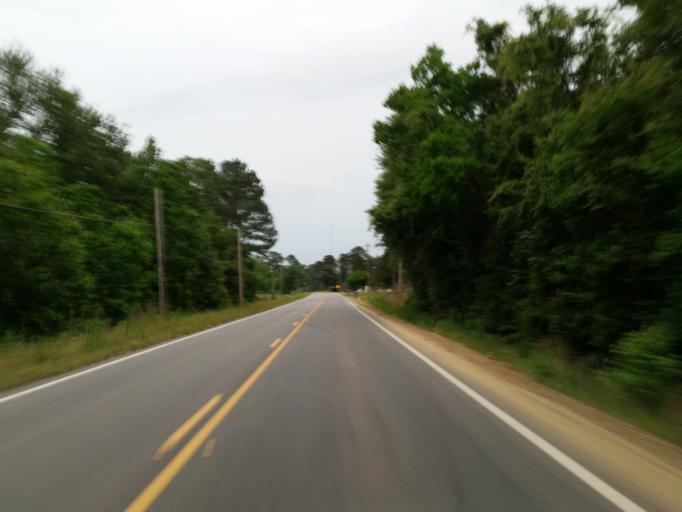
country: US
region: Georgia
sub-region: Crisp County
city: Cordele
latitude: 31.9400
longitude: -83.7809
